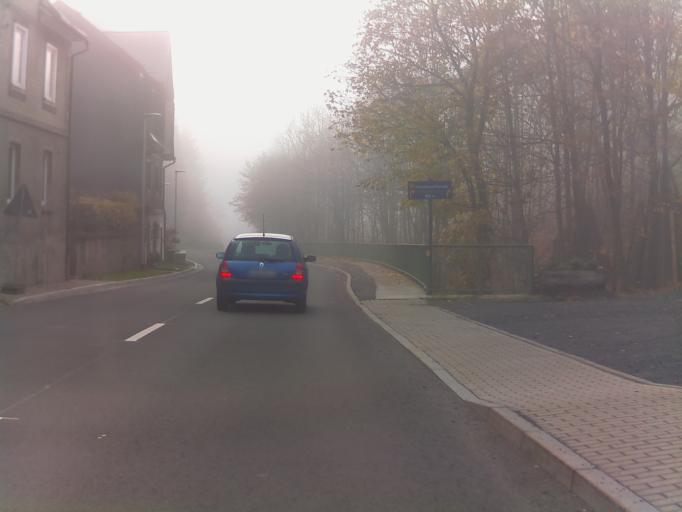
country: DE
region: Thuringia
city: Lauscha
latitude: 50.4654
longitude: 11.1592
